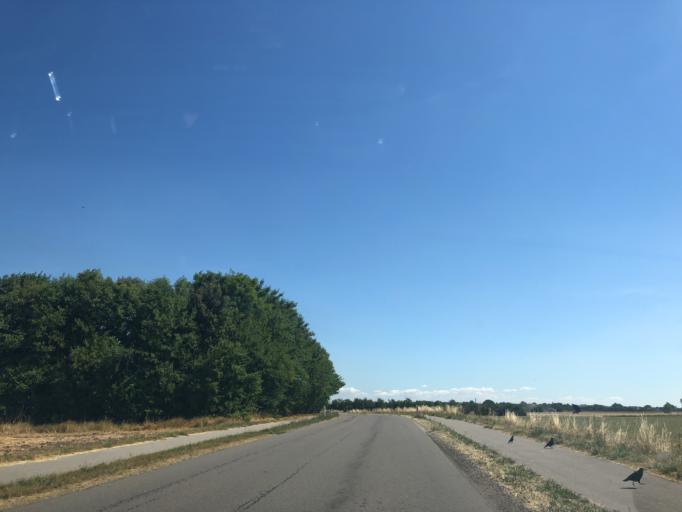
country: DK
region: Zealand
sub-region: Slagelse Kommune
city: Forlev
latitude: 55.3745
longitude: 11.2392
